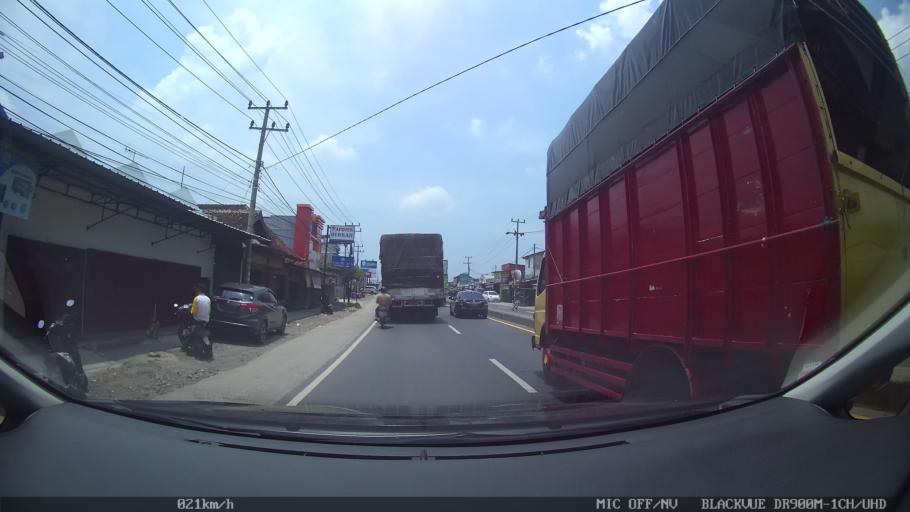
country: ID
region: Lampung
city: Natar
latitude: -5.3182
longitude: 105.1967
